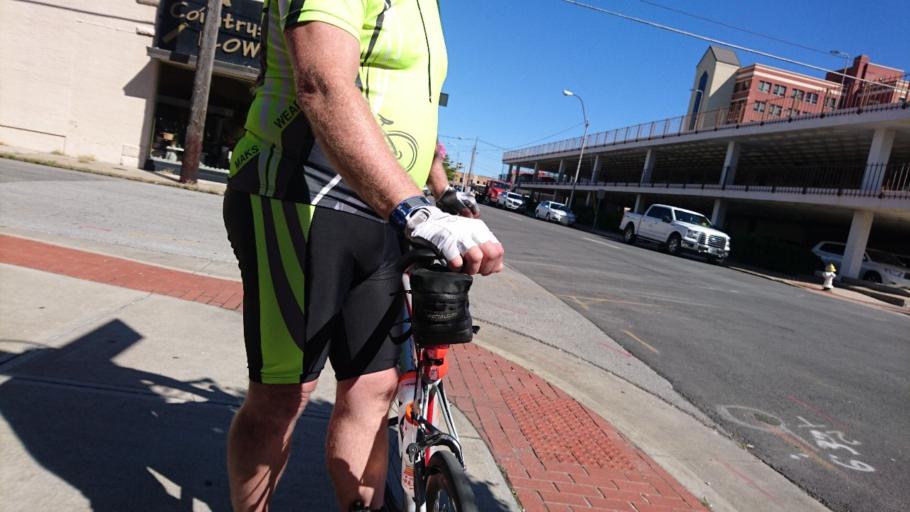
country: US
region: Missouri
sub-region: Jasper County
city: Joplin
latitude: 37.0867
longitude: -94.5146
